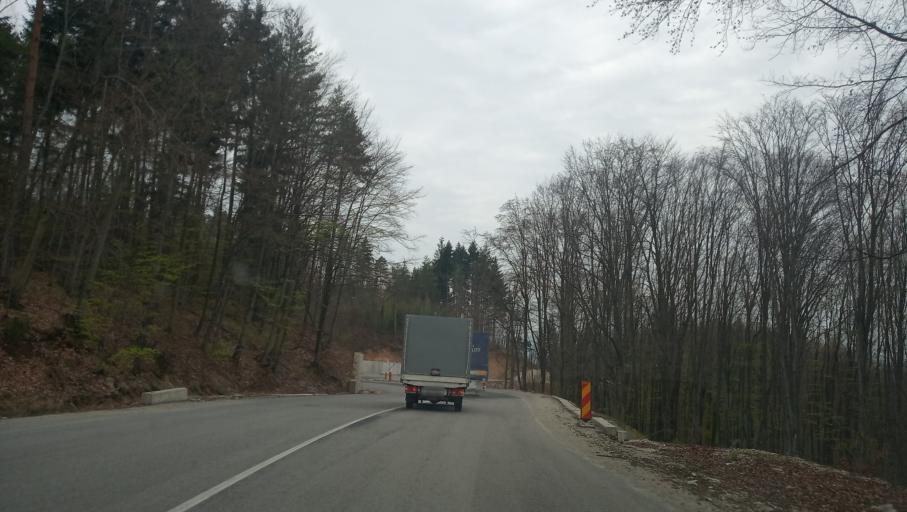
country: RO
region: Bihor
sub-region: Comuna Cristioru de Jos
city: Cristioru de Jos
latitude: 46.3878
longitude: 22.5559
